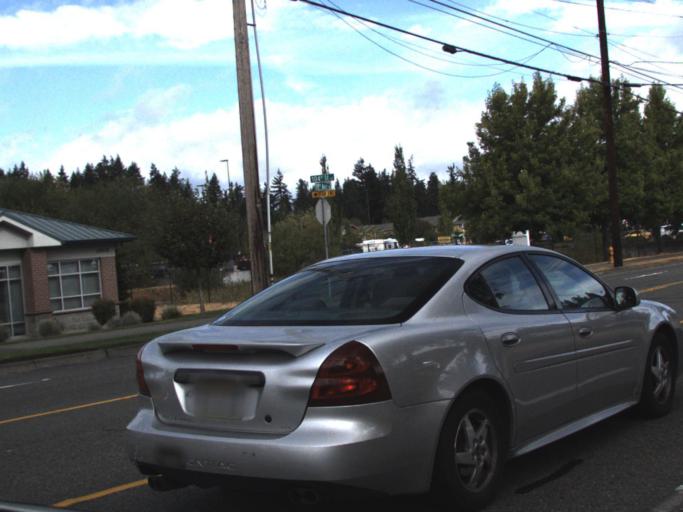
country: US
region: Washington
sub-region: Snohomish County
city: Mill Creek
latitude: 47.9035
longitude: -122.2069
